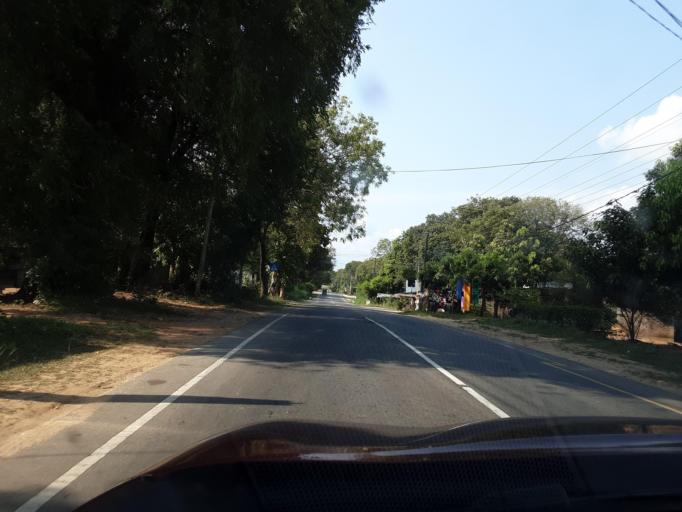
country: LK
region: Uva
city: Haputale
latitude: 6.5902
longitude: 81.1416
